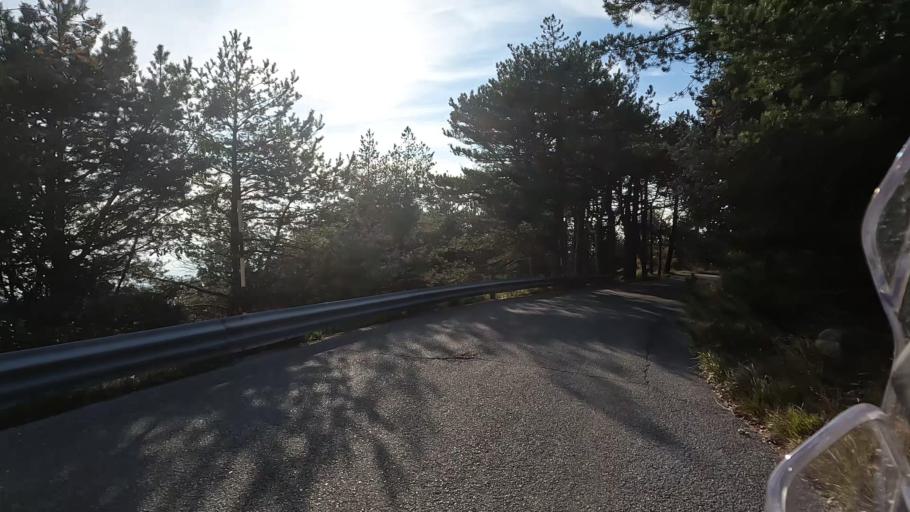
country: IT
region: Liguria
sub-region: Provincia di Savona
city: San Giovanni
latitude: 44.4284
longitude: 8.5484
